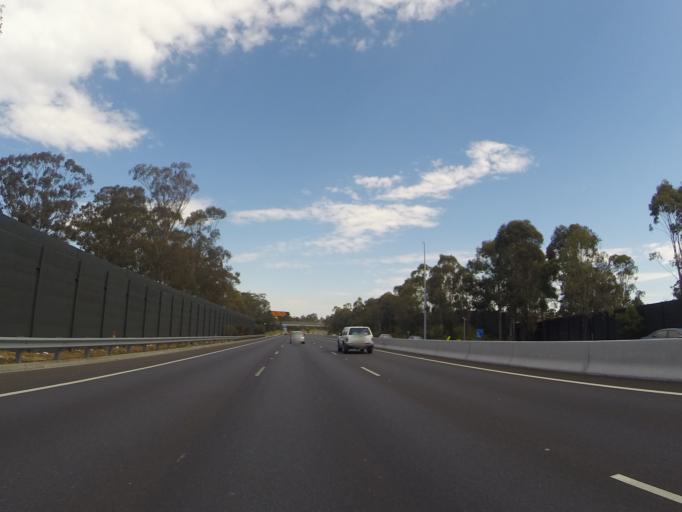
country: AU
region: New South Wales
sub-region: Campbelltown Municipality
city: Glenfield
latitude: -33.9440
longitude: 150.8989
